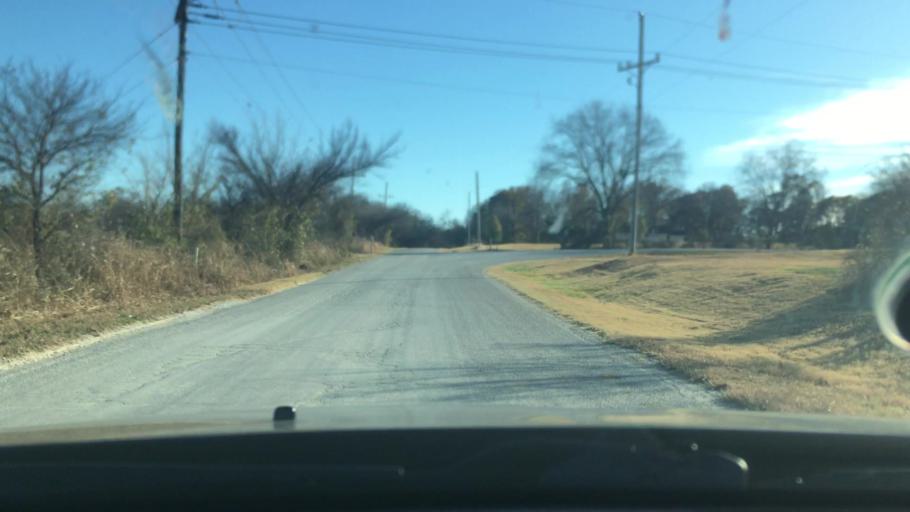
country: US
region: Oklahoma
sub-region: Murray County
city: Davis
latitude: 34.4907
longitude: -97.1575
